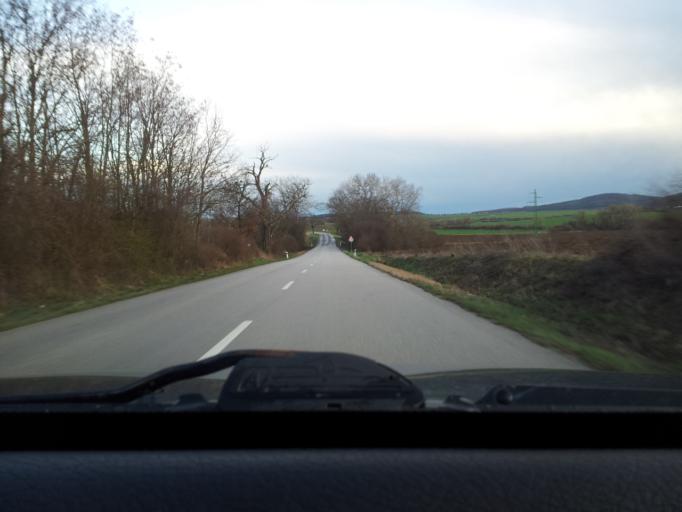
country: SK
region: Nitriansky
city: Tlmace
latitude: 48.3291
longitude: 18.4969
